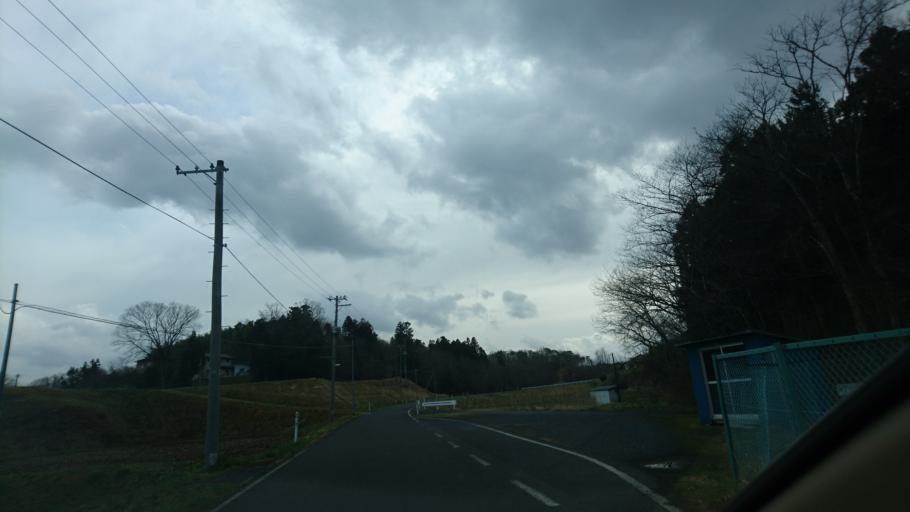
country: JP
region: Iwate
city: Ichinoseki
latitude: 38.8851
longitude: 141.1675
